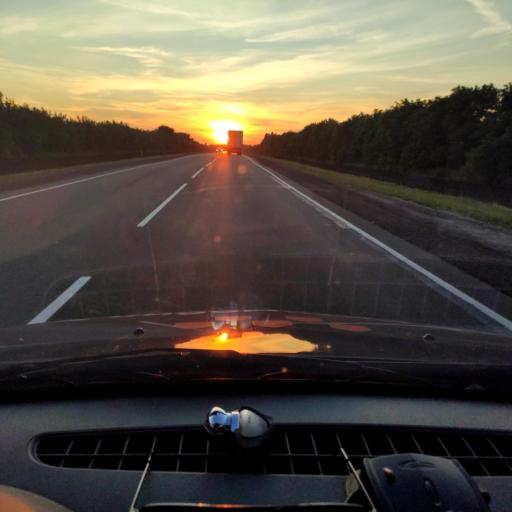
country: RU
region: Voronezj
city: Nizhnedevitsk
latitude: 51.5687
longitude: 38.3384
